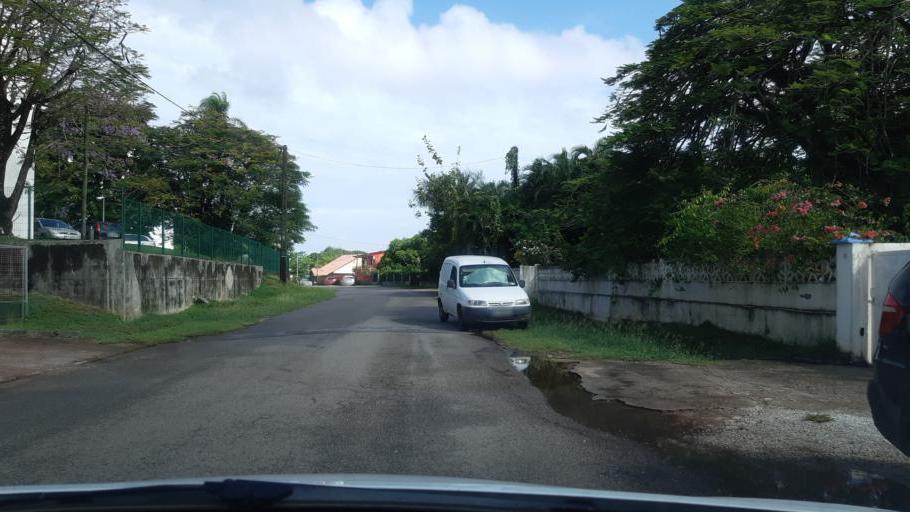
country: GF
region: Guyane
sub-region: Guyane
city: Cayenne
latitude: 4.9410
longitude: -52.3175
